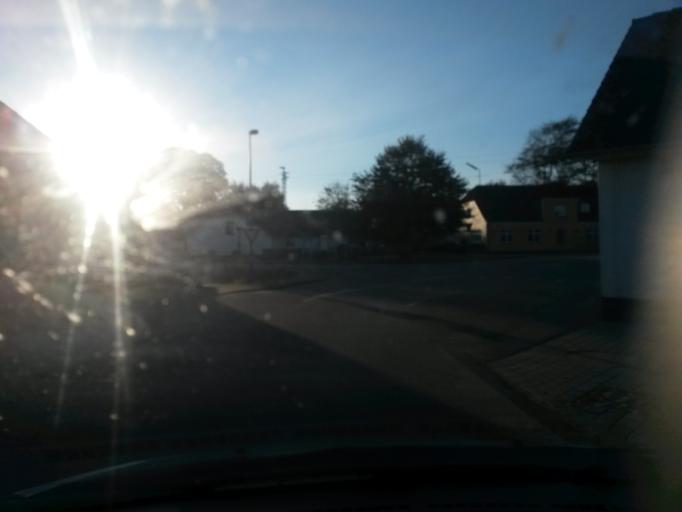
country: DK
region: Central Jutland
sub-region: Silkeborg Kommune
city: Kjellerup
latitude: 56.2740
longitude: 9.3141
